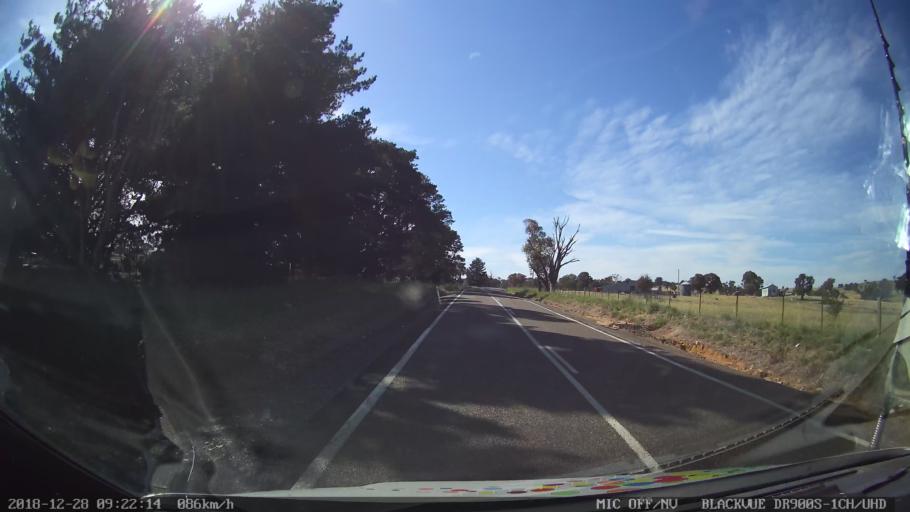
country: AU
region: New South Wales
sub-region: Upper Lachlan Shire
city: Crookwell
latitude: -34.3714
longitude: 149.3803
